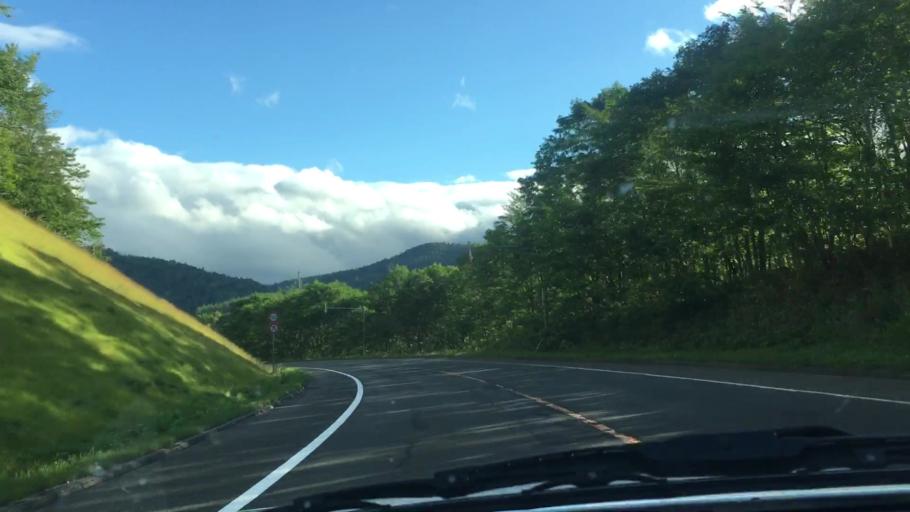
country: JP
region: Hokkaido
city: Shimo-furano
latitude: 43.1280
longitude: 142.6782
